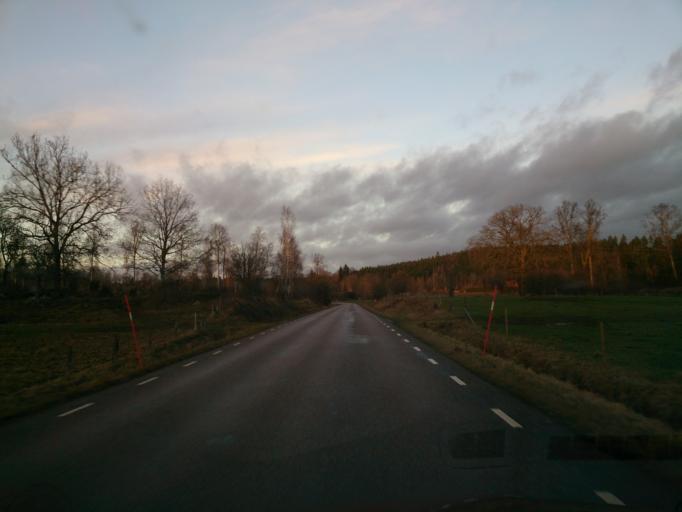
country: SE
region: OEstergoetland
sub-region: Atvidabergs Kommun
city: Atvidaberg
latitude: 58.3300
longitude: 16.0271
